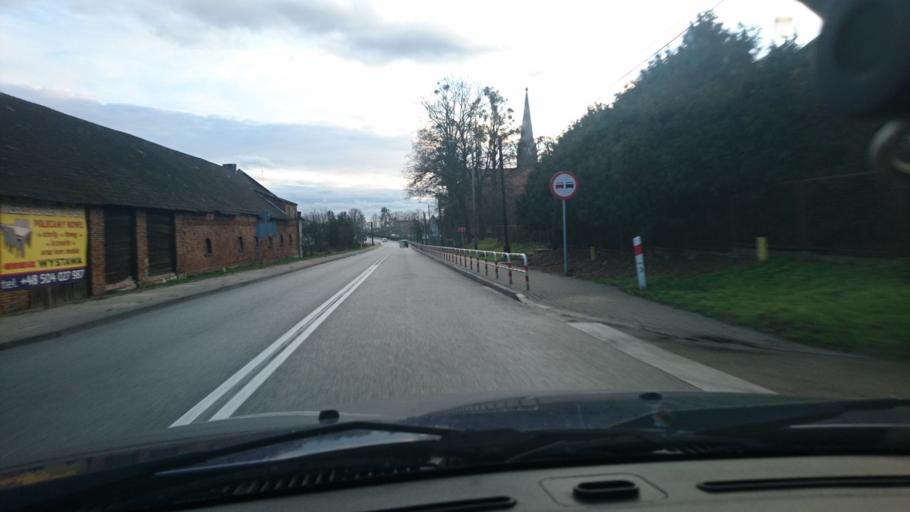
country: PL
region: Opole Voivodeship
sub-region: Powiat kluczborski
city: Kluczbork
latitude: 51.0297
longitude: 18.1923
